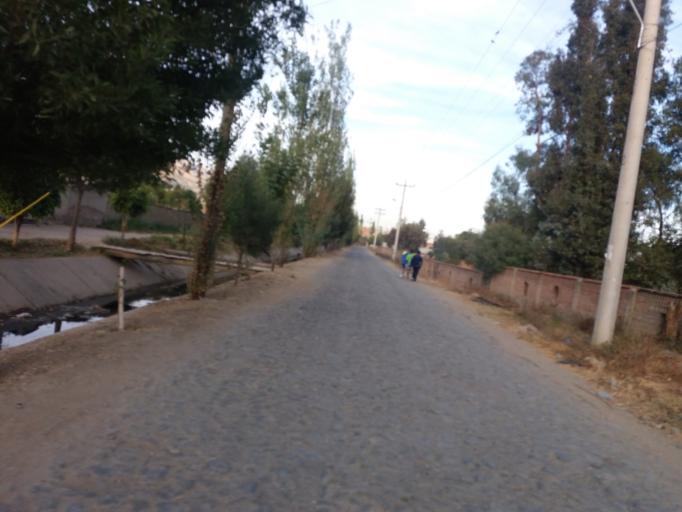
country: BO
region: Cochabamba
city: Cochabamba
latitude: -17.3568
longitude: -66.1971
